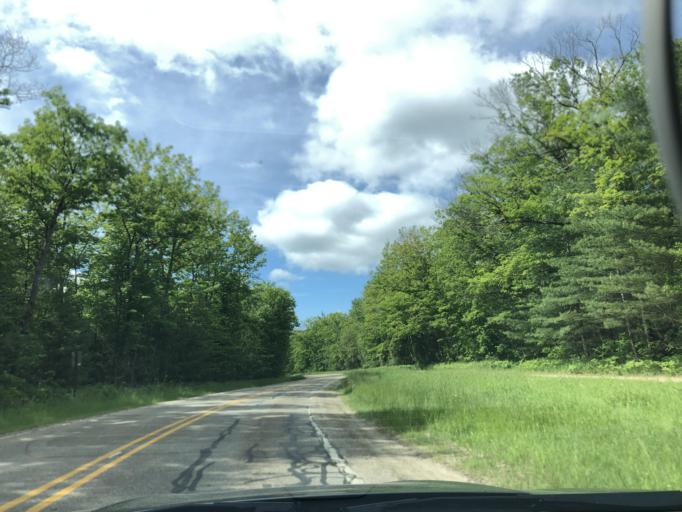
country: US
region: Michigan
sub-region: Roscommon County
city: Houghton Lake
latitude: 44.3501
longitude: -84.8537
